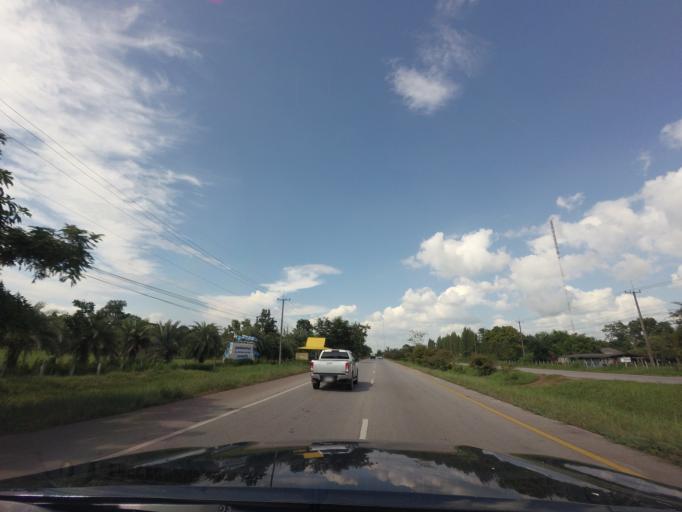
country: TH
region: Nong Khai
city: Sa Khrai
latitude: 17.6528
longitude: 102.7882
